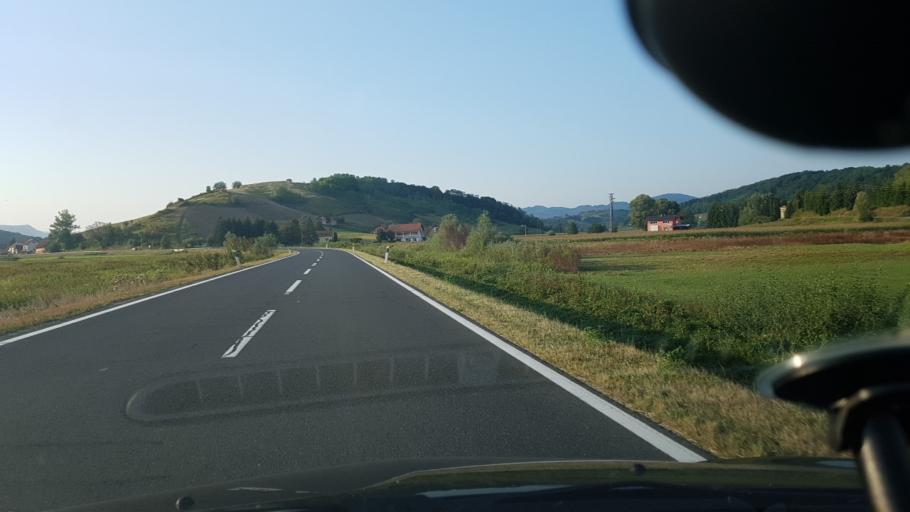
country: HR
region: Krapinsko-Zagorska
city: Pregrada
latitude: 46.1101
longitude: 15.8133
